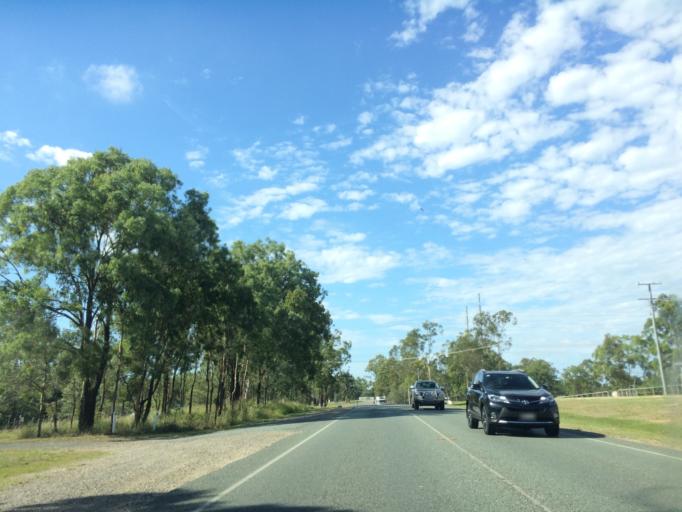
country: AU
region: Queensland
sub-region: Logan
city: Park Ridge South
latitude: -27.7269
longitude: 152.9844
